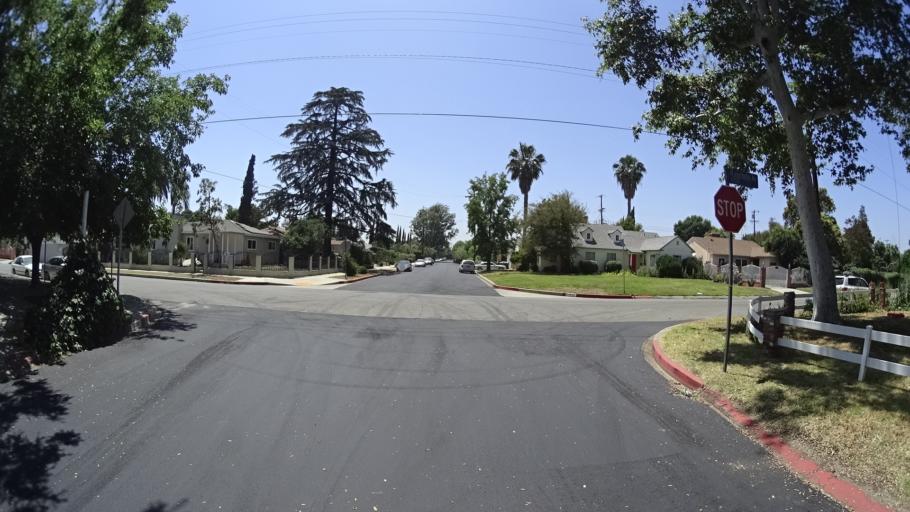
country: US
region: California
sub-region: Los Angeles County
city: Van Nuys
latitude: 34.1886
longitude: -118.4354
